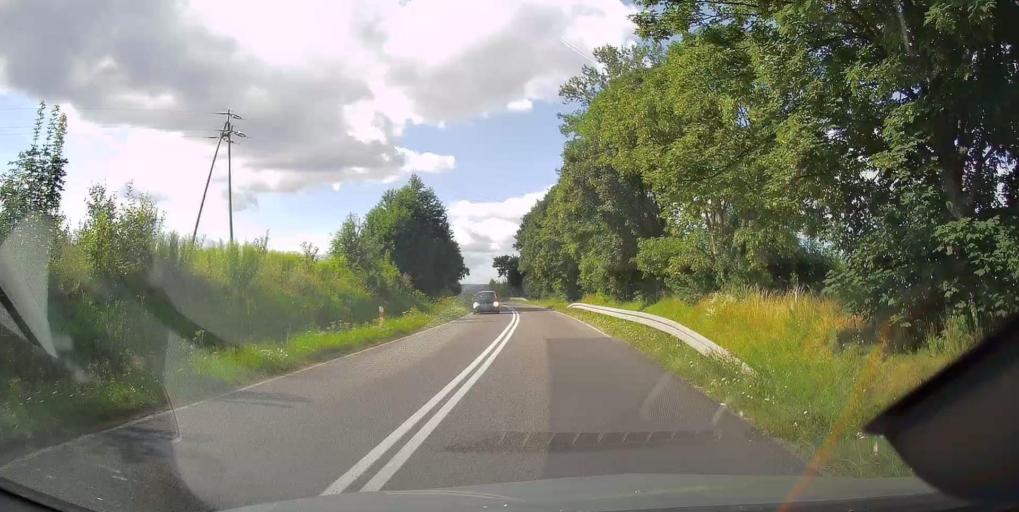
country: PL
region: Swietokrzyskie
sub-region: Powiat kielecki
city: Nowa Slupia
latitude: 50.8872
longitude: 21.0452
